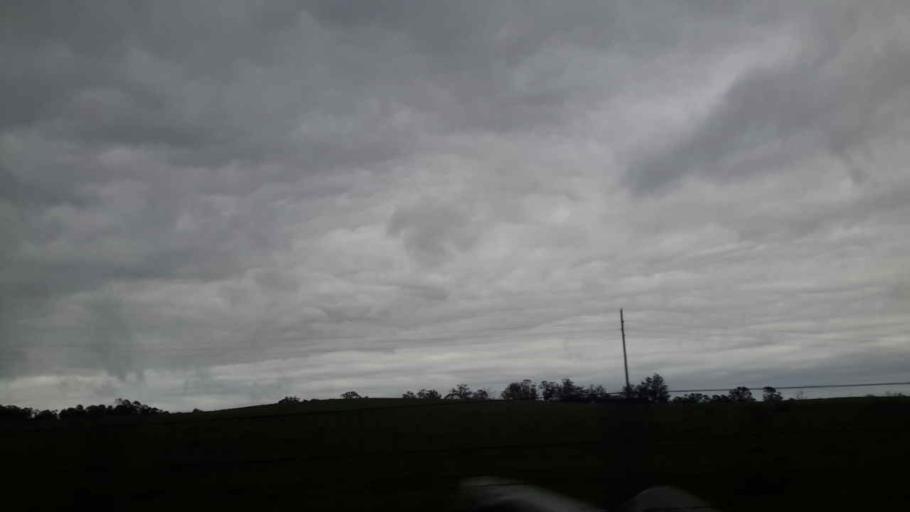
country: AU
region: New South Wales
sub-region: Wollondilly
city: Douglas Park
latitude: -34.2135
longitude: 150.7216
